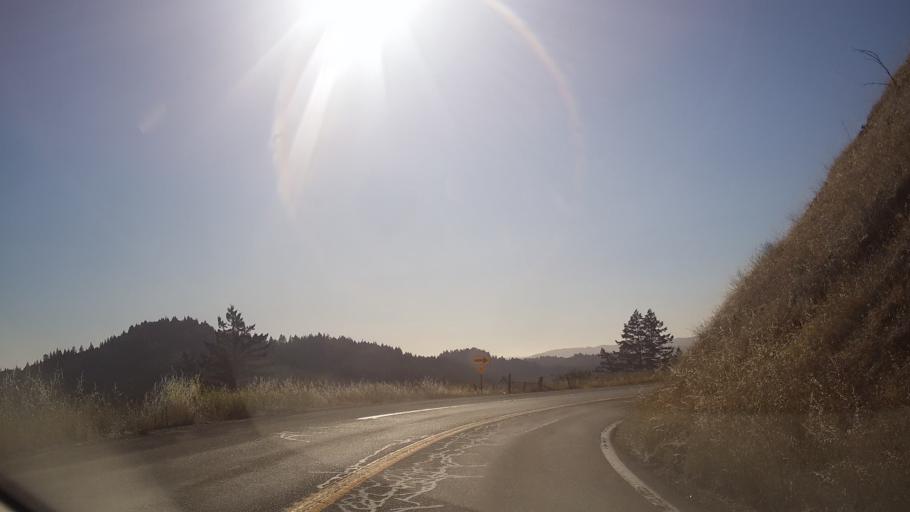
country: US
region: California
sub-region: Mendocino County
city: Brooktrails
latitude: 39.3908
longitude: -123.4457
